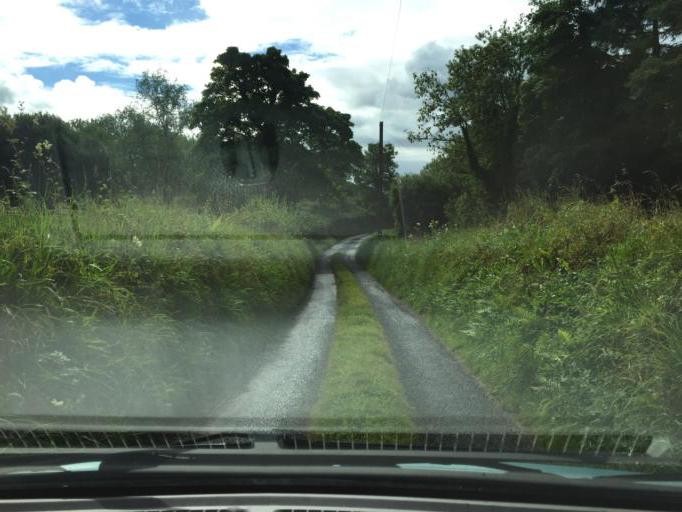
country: IE
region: Connaught
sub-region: Maigh Eo
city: Swinford
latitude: 54.0354
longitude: -8.9002
